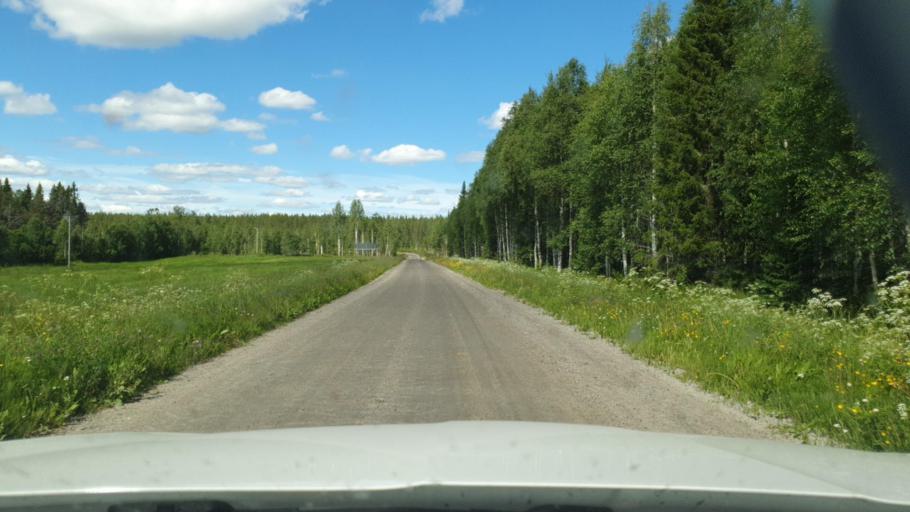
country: SE
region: Vaesterbotten
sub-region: Skelleftea Kommun
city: Backa
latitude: 65.1574
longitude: 21.1588
